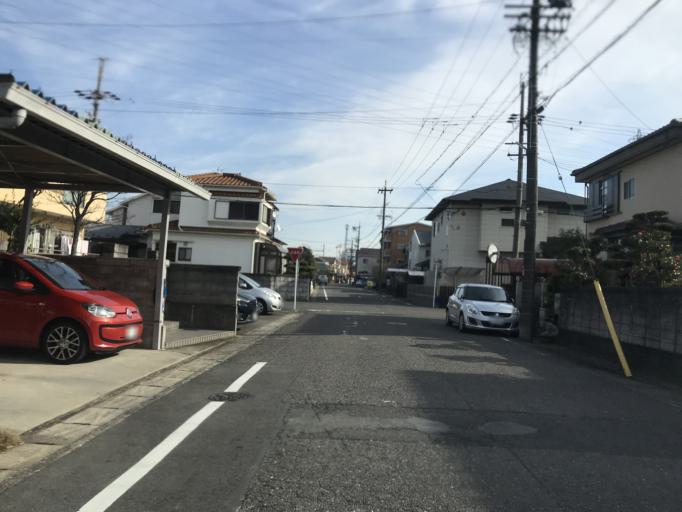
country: JP
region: Aichi
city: Inazawa
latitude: 35.2209
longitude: 136.8332
